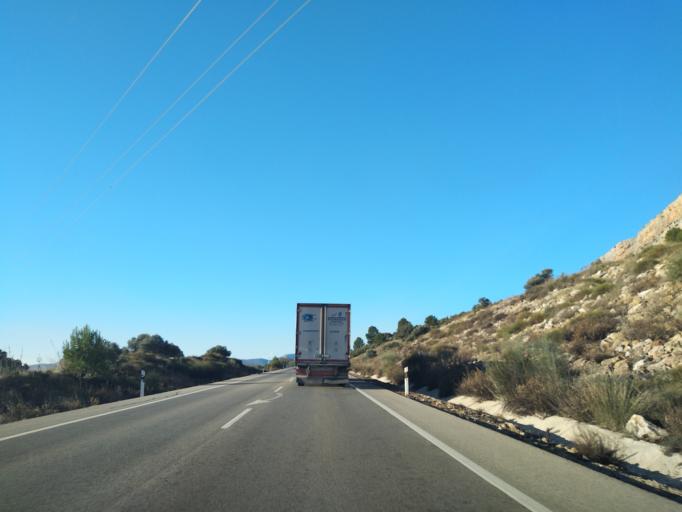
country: ES
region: Andalusia
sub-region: Provincia de Malaga
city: Campillos
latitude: 36.9730
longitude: -4.8371
